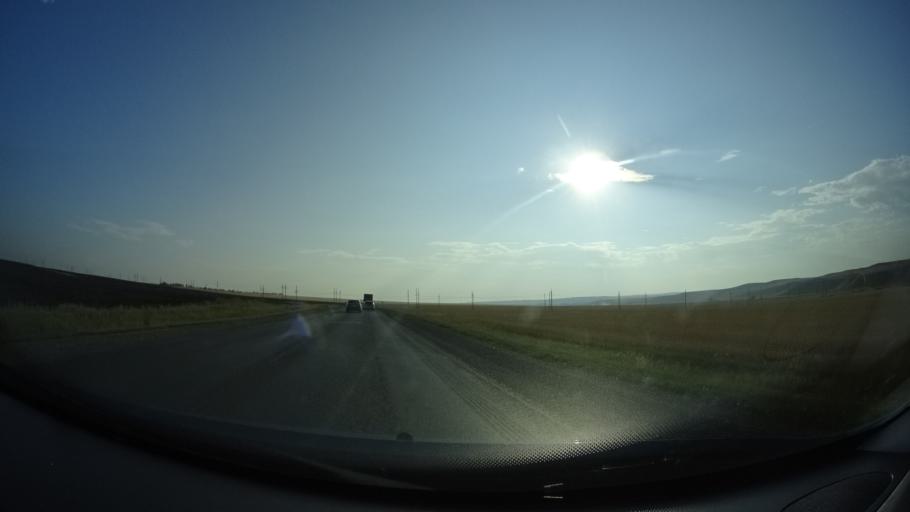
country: RU
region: Orenburg
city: Severnoye
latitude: 54.1287
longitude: 52.5763
